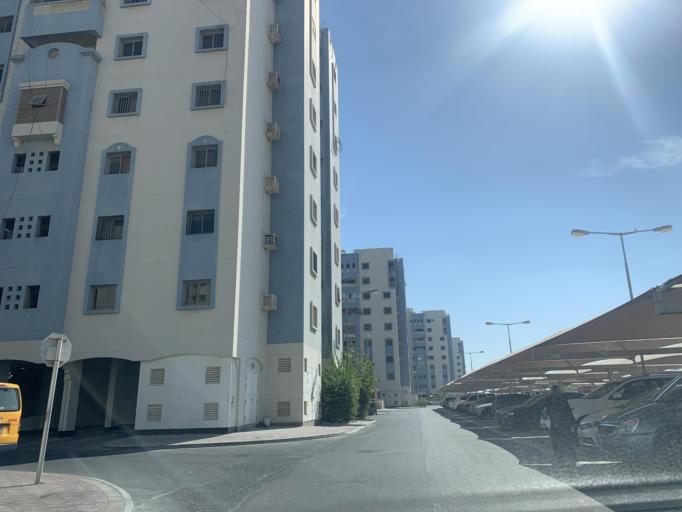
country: BH
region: Central Governorate
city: Madinat Hamad
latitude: 26.1154
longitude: 50.4900
